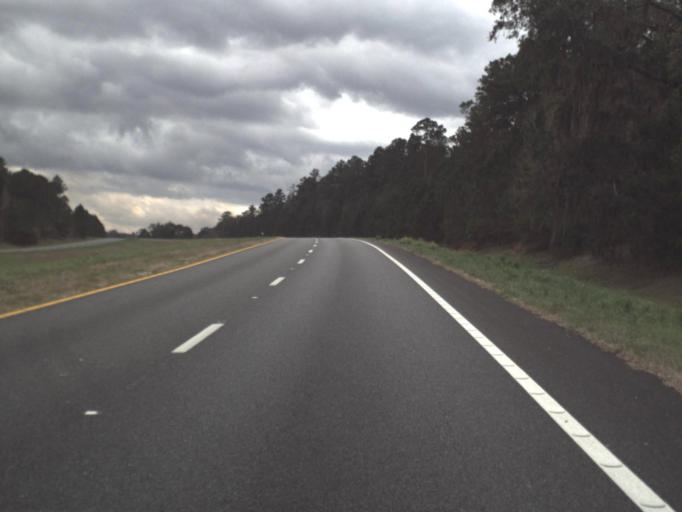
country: US
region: Georgia
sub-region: Grady County
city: Cairo
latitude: 30.6588
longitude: -84.1693
